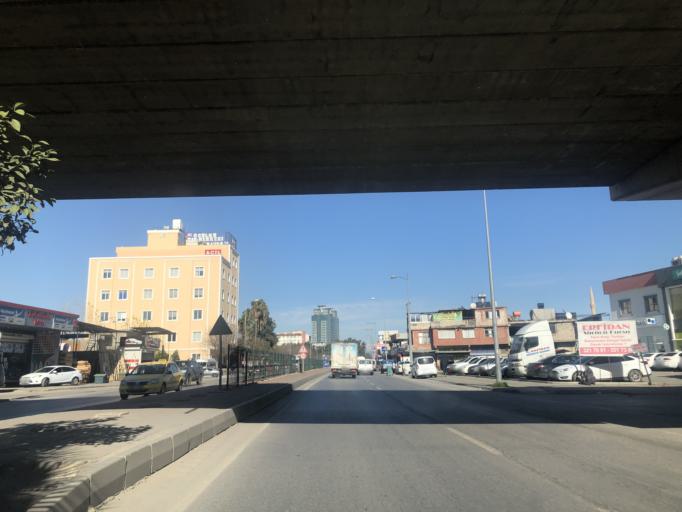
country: TR
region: Adana
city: Yuregir
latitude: 36.9809
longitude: 35.3385
